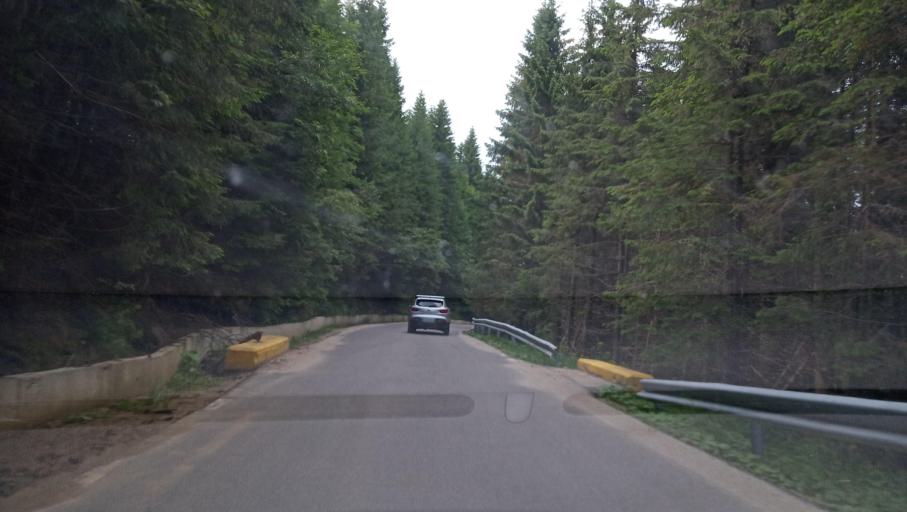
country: RO
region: Dambovita
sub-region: Comuna Moroeni
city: Glod
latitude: 45.3249
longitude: 25.4485
